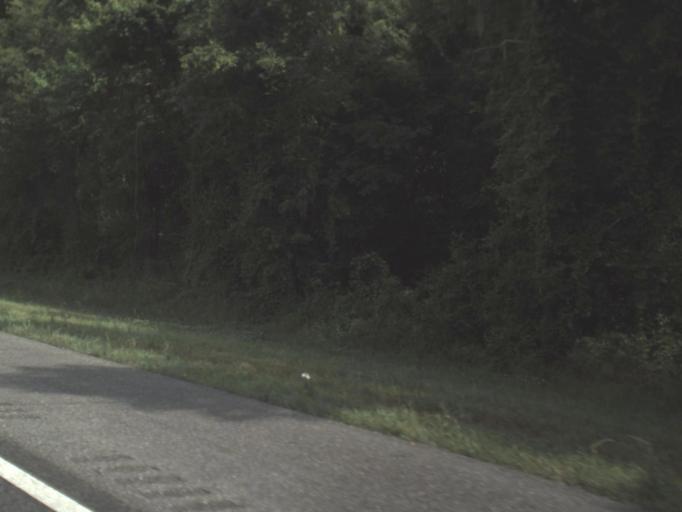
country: US
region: Florida
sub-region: Suwannee County
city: Live Oak
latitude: 30.2952
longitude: -82.8920
